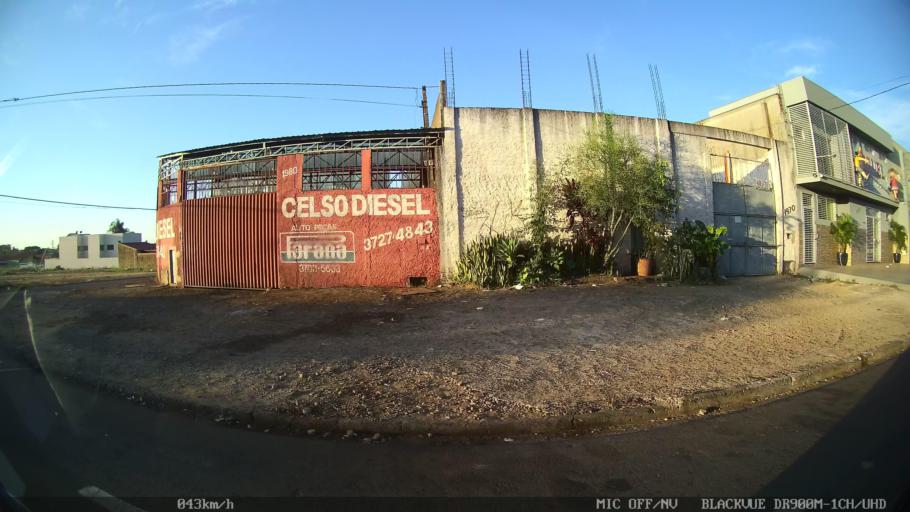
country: BR
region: Sao Paulo
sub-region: Franca
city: Franca
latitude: -20.5055
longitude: -47.3960
